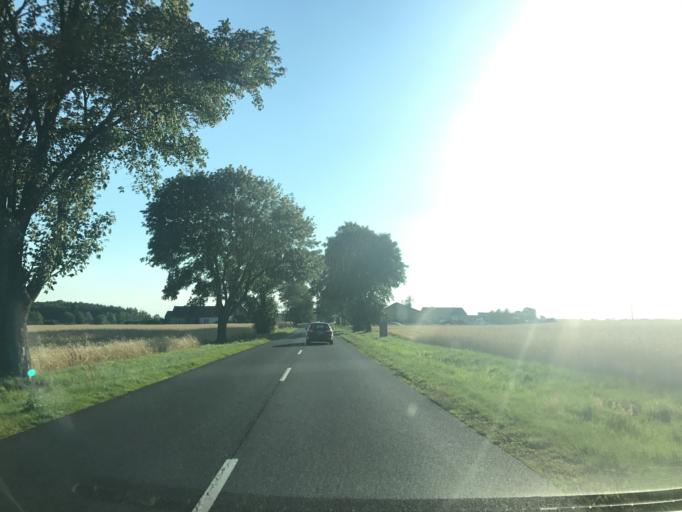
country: PL
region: Greater Poland Voivodeship
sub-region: Powiat koninski
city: Grodziec
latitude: 52.0493
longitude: 18.1060
